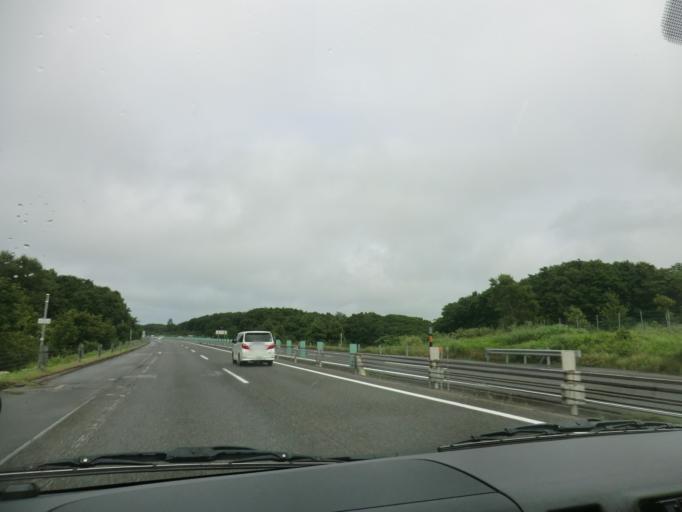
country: JP
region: Hokkaido
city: Chitose
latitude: 42.8280
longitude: 141.6136
